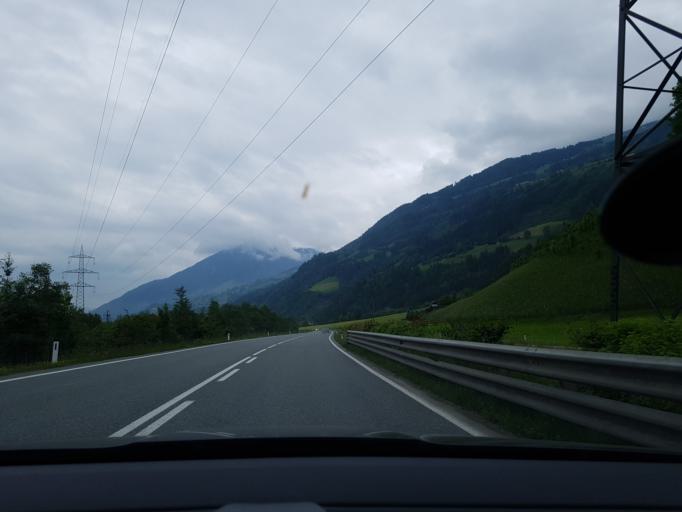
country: AT
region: Tyrol
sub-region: Politischer Bezirk Schwaz
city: Rohrberg
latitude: 47.2487
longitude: 11.9014
